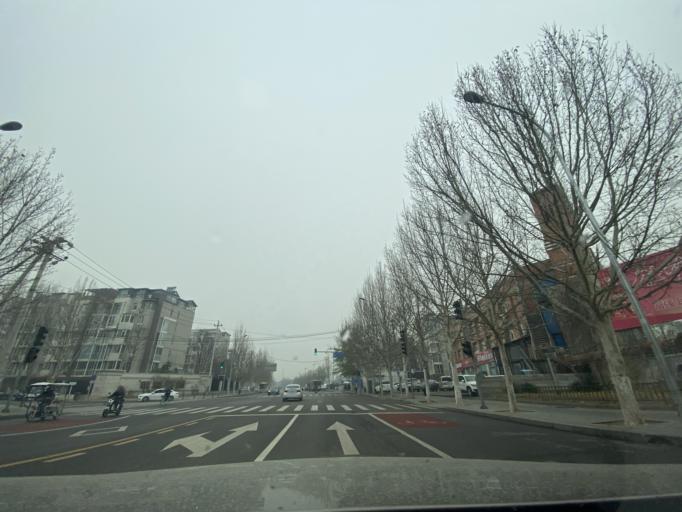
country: CN
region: Beijing
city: Sijiqing
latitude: 39.9661
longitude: 116.2415
